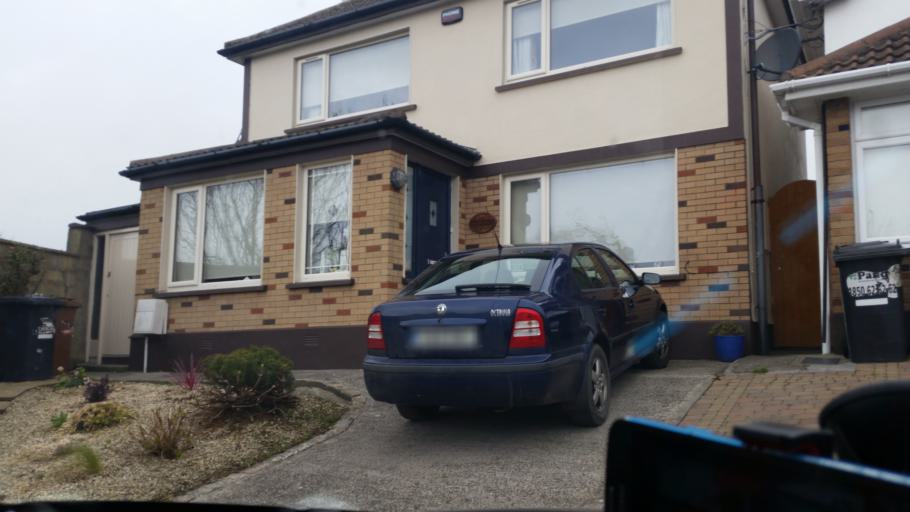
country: IE
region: Leinster
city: Portmarnock
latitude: 53.4230
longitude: -6.1375
